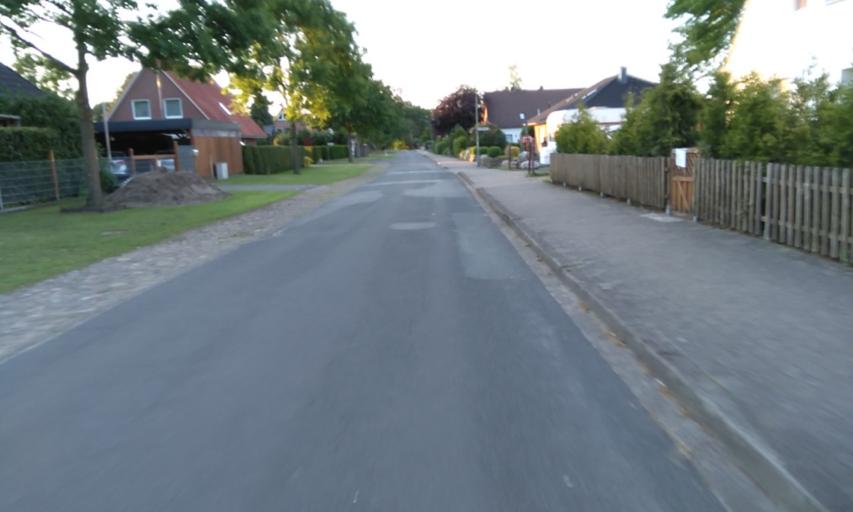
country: DE
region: Lower Saxony
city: Ahlerstedt
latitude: 53.4272
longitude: 9.4285
